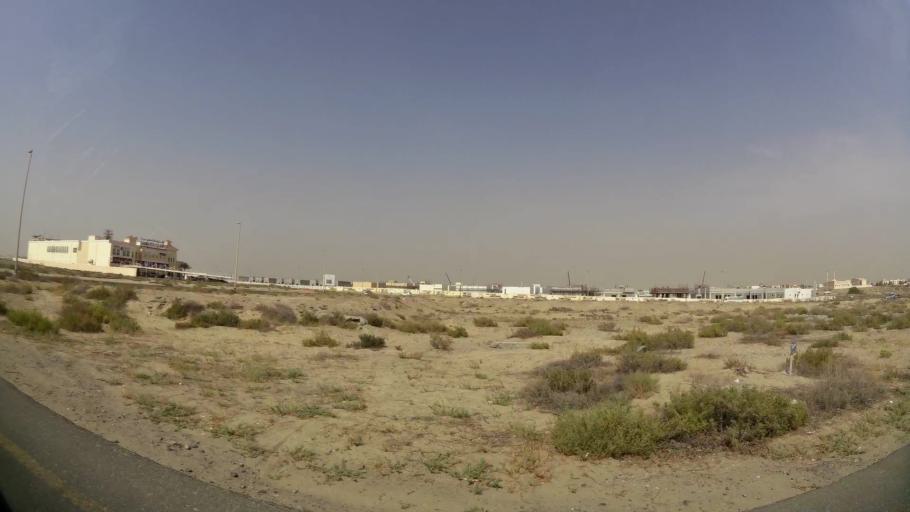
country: AE
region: Ash Shariqah
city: Sharjah
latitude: 25.2595
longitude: 55.4396
